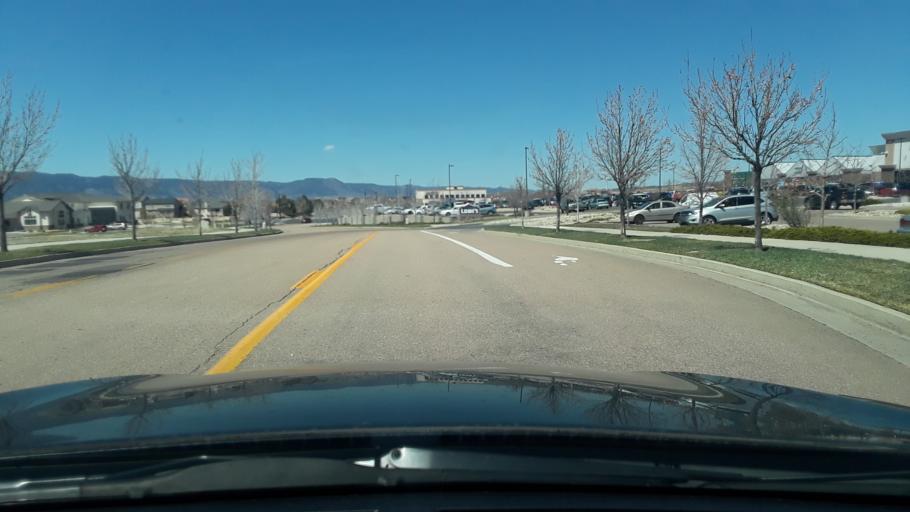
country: US
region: Colorado
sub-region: El Paso County
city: Black Forest
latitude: 38.9694
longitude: -104.7490
